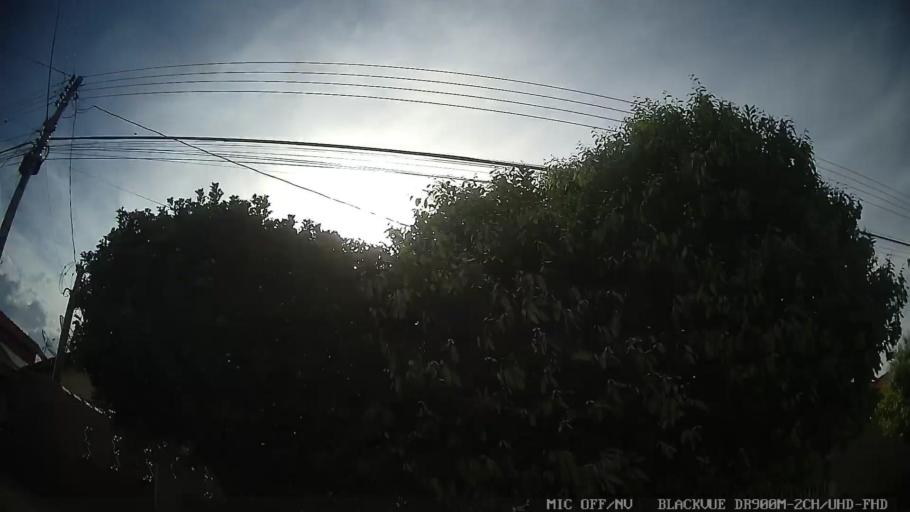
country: BR
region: Sao Paulo
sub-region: Jaguariuna
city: Jaguariuna
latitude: -22.6394
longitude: -47.0561
